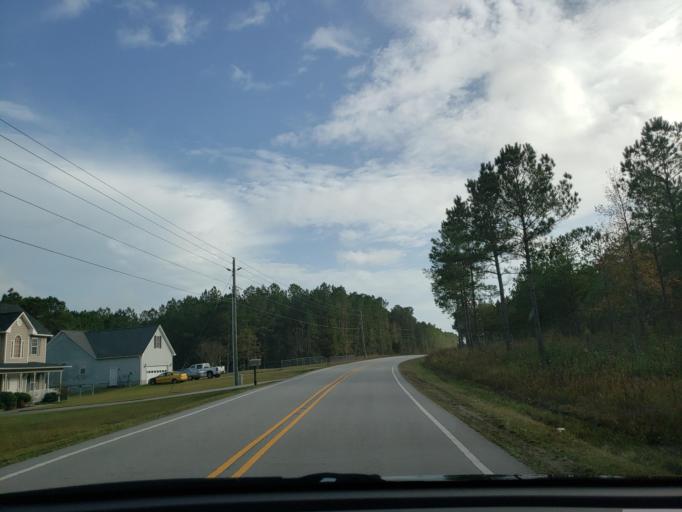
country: US
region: North Carolina
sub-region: Onslow County
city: Jacksonville
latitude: 34.6803
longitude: -77.5037
